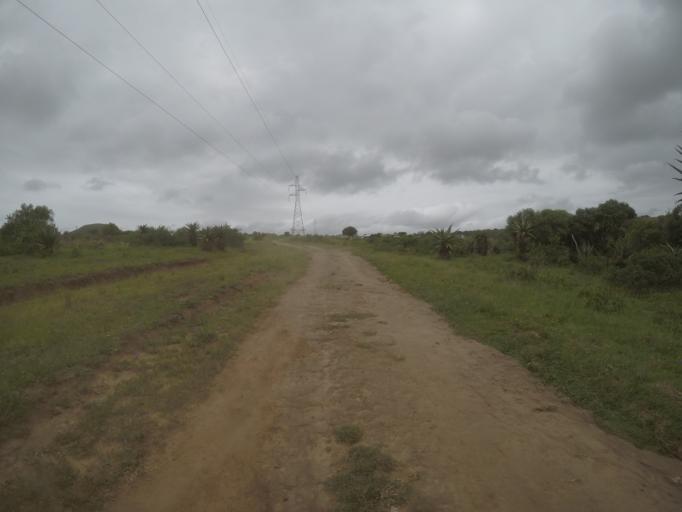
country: ZA
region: KwaZulu-Natal
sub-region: uThungulu District Municipality
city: Empangeni
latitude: -28.5984
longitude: 31.8452
